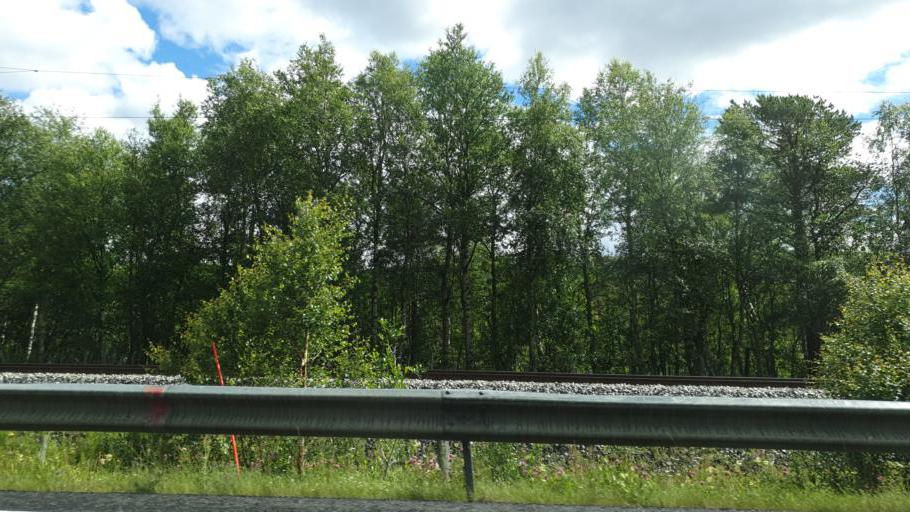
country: NO
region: Sor-Trondelag
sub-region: Oppdal
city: Oppdal
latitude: 62.6138
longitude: 9.7522
